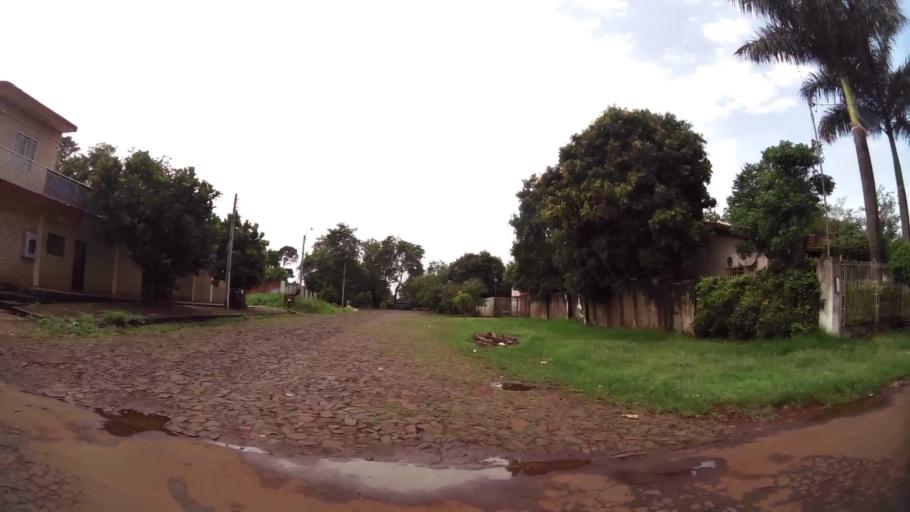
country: PY
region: Alto Parana
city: Ciudad del Este
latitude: -25.5032
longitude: -54.6661
